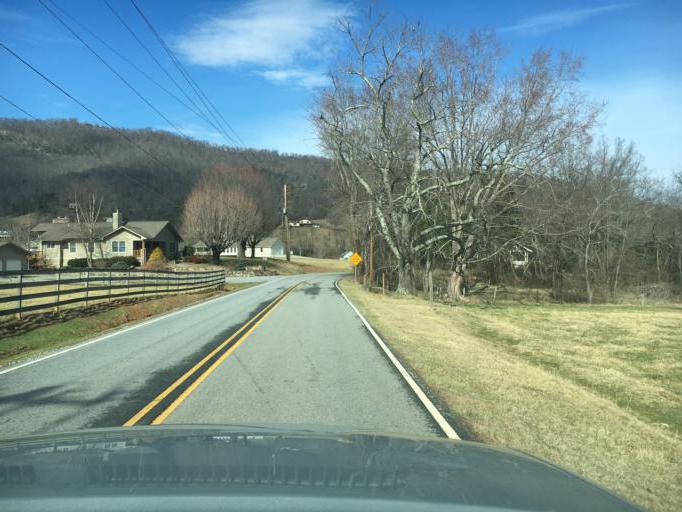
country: US
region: North Carolina
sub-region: Haywood County
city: Clyde
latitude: 35.4884
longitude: -82.8862
